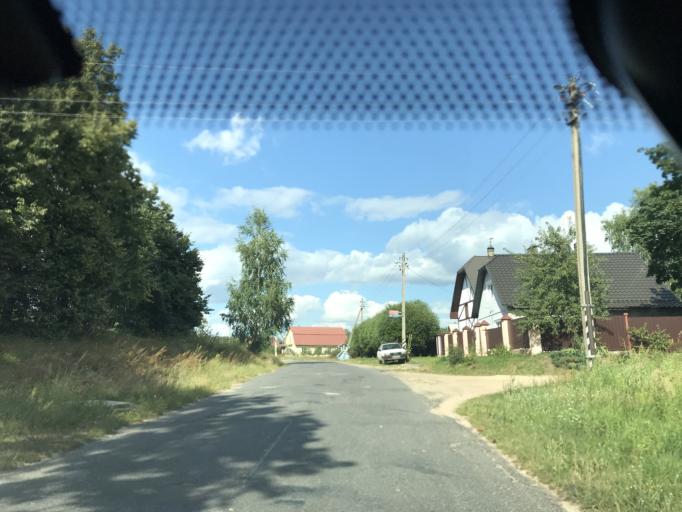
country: BY
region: Mogilev
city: Poselok Voskhod
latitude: 53.7900
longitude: 30.3593
